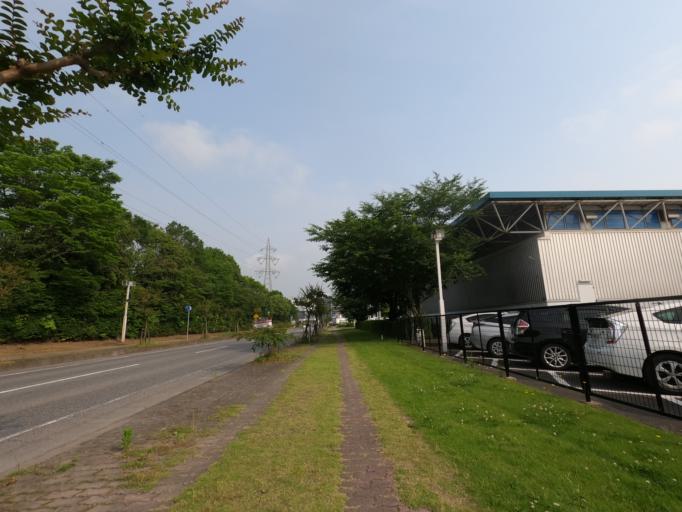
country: JP
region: Ibaraki
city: Moriya
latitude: 35.9548
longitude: 139.9631
